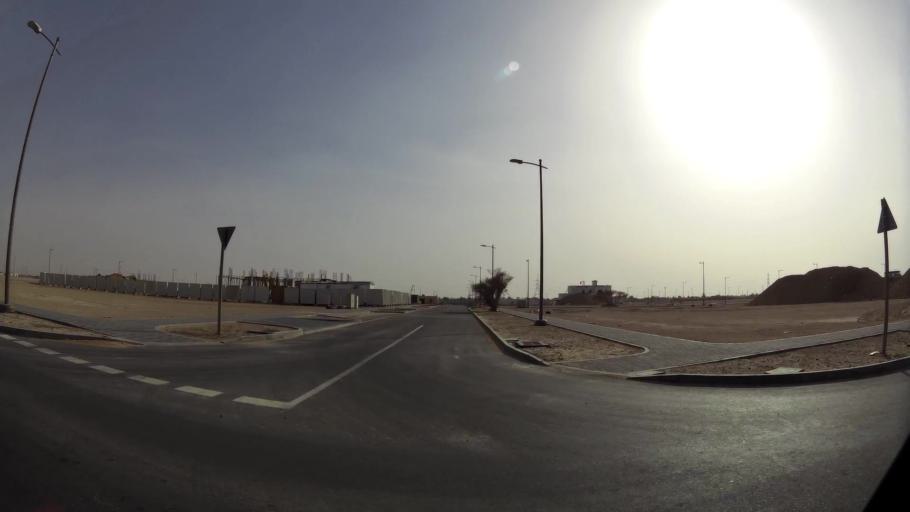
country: AE
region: Abu Dhabi
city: Al Ain
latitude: 24.1218
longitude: 55.7227
